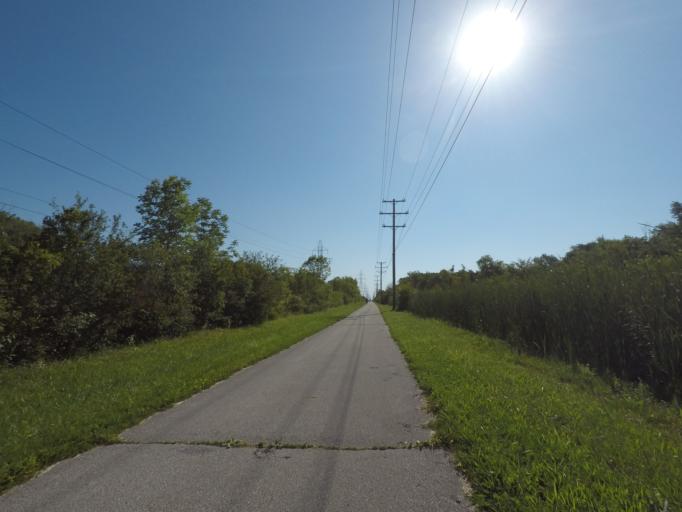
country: US
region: Wisconsin
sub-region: Waukesha County
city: Waukesha
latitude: 43.0099
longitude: -88.1961
